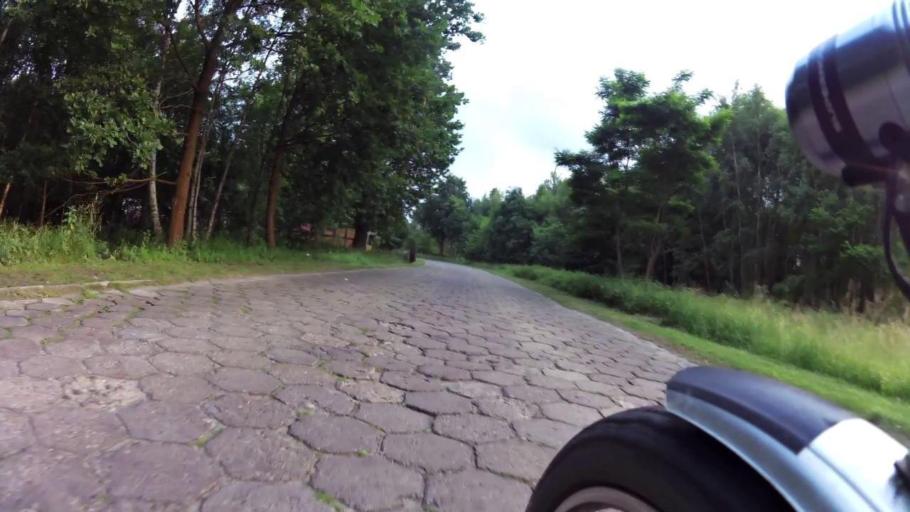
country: PL
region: West Pomeranian Voivodeship
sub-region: Powiat policki
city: Police
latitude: 53.6566
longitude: 14.4955
